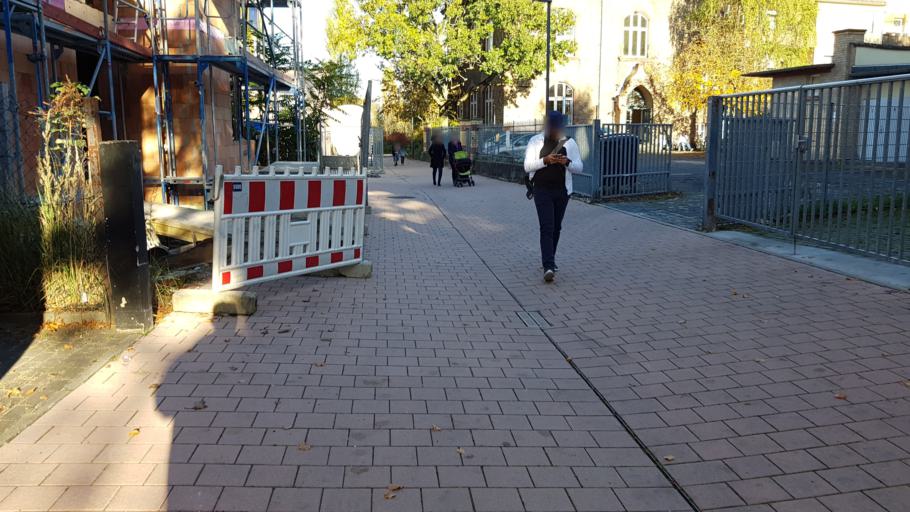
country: DE
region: Hesse
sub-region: Regierungsbezirk Darmstadt
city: Offenbach
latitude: 50.1217
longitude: 8.7723
